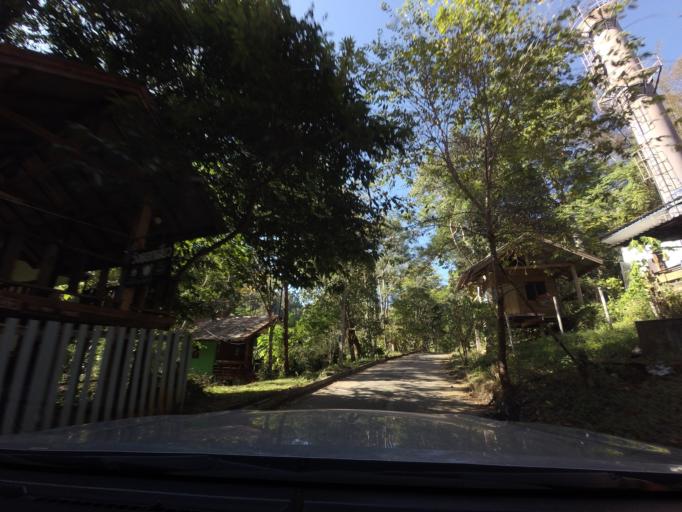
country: TH
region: Lampang
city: Mueang Pan
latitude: 18.8293
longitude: 99.3830
